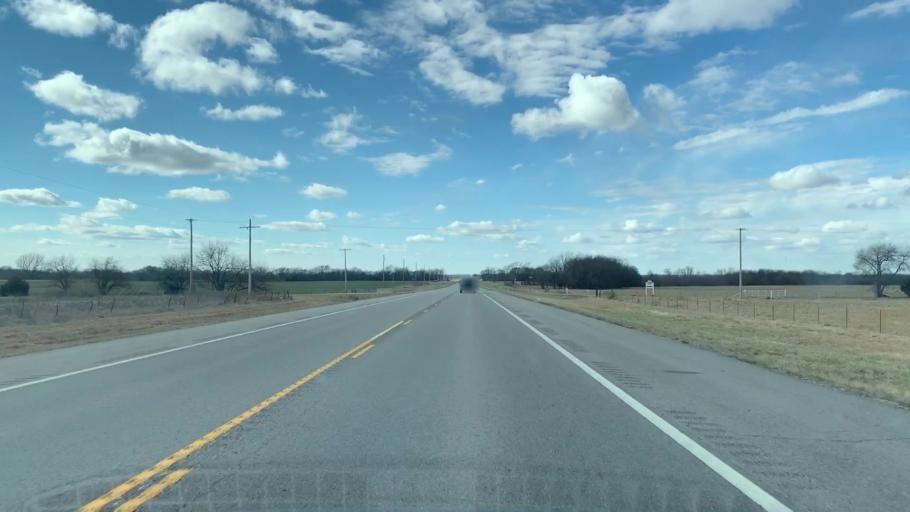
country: US
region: Kansas
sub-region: Labette County
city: Oswego
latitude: 37.3401
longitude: -95.0301
